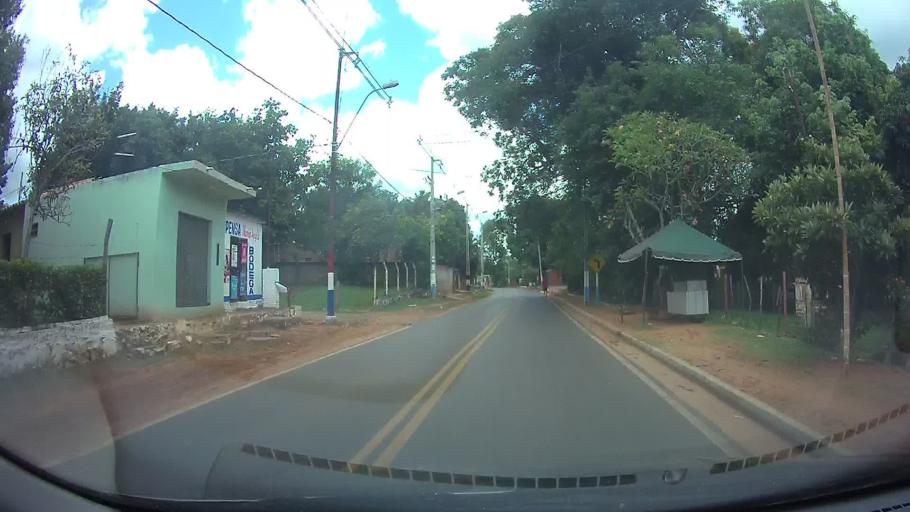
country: PY
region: Central
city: Capiata
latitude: -25.2971
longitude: -57.4413
